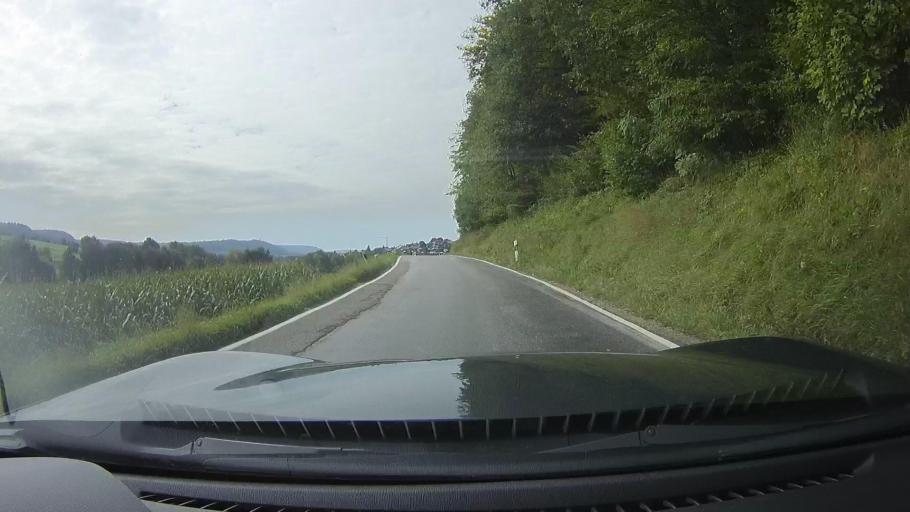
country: DE
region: Baden-Wuerttemberg
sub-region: Regierungsbezirk Stuttgart
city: Beilstein
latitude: 49.0490
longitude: 9.3362
